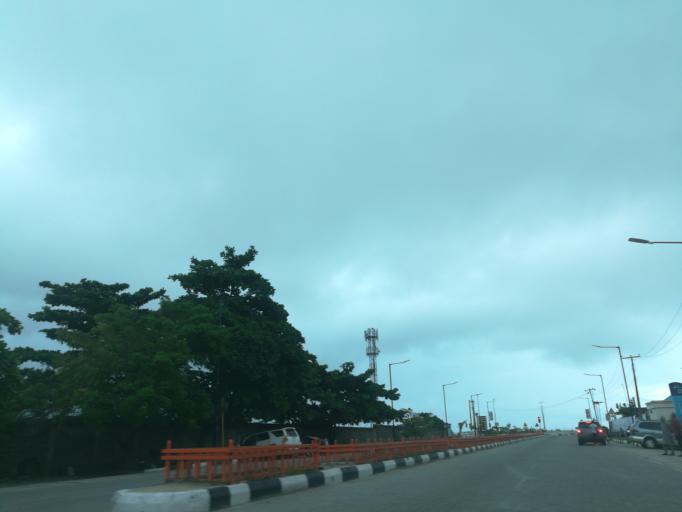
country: NG
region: Lagos
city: Ikoyi
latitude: 6.4239
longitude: 3.4238
